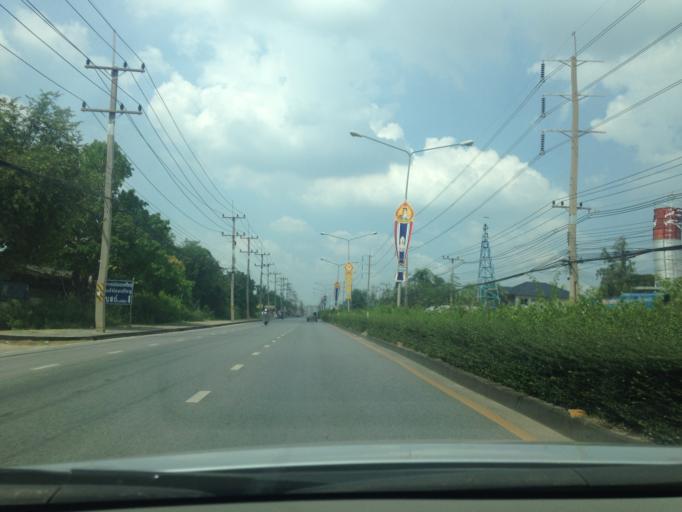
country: TH
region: Pathum Thani
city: Sam Khok
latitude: 14.0528
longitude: 100.5245
